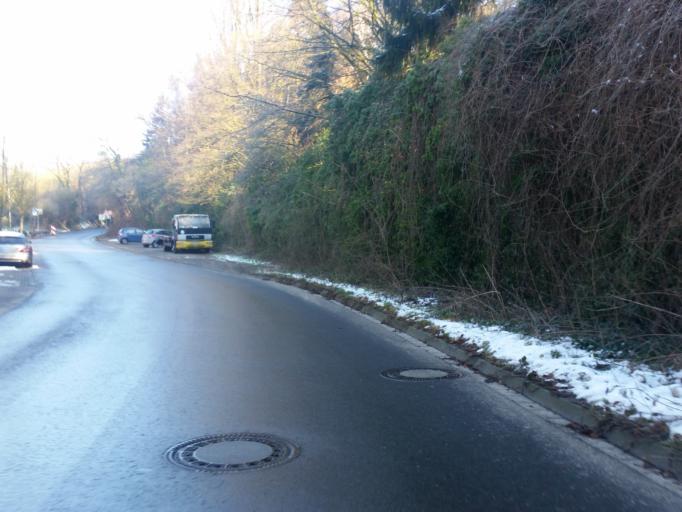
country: DE
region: North Rhine-Westphalia
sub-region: Regierungsbezirk Koln
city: Wurselen
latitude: 50.7887
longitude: 6.1563
